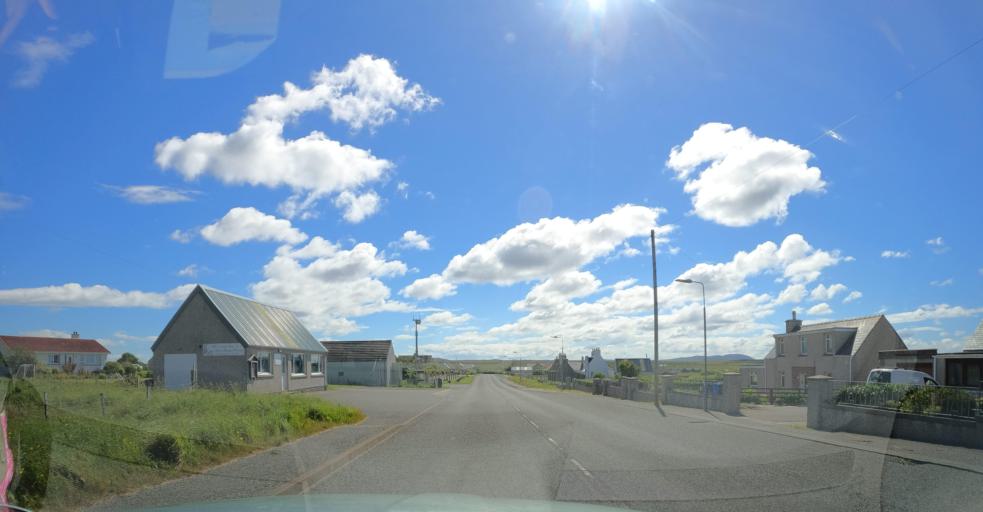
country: GB
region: Scotland
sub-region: Eilean Siar
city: Isle of Lewis
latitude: 58.3575
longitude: -6.5134
